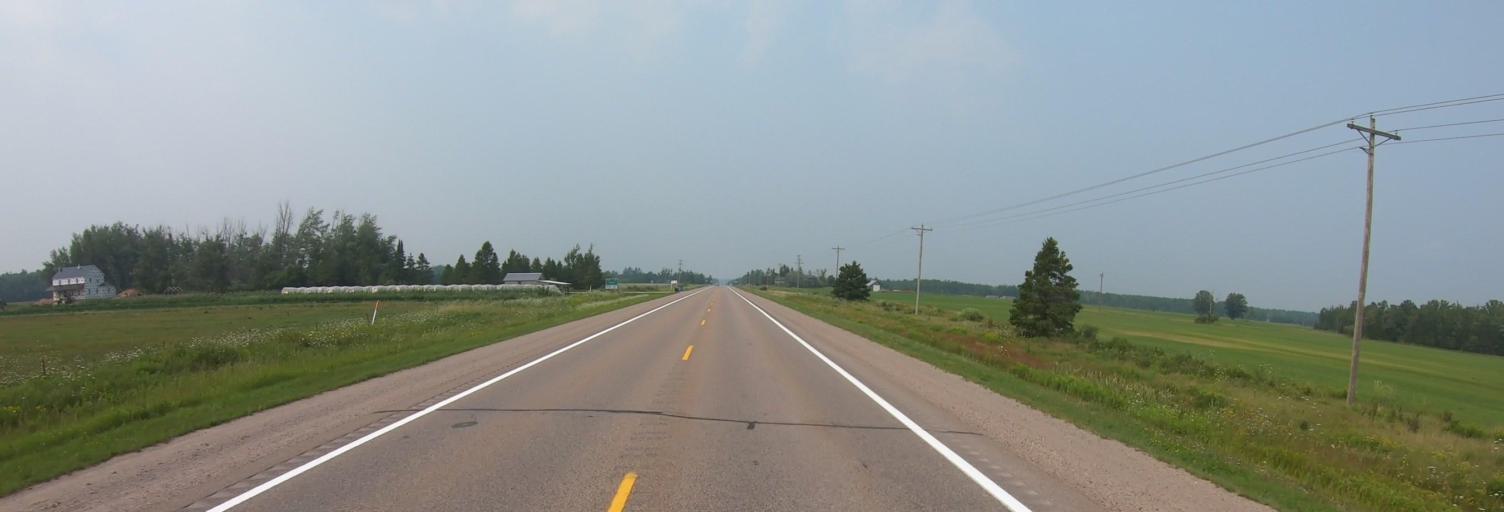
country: US
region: Michigan
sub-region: Chippewa County
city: Sault Ste. Marie
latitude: 46.3245
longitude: -84.3639
